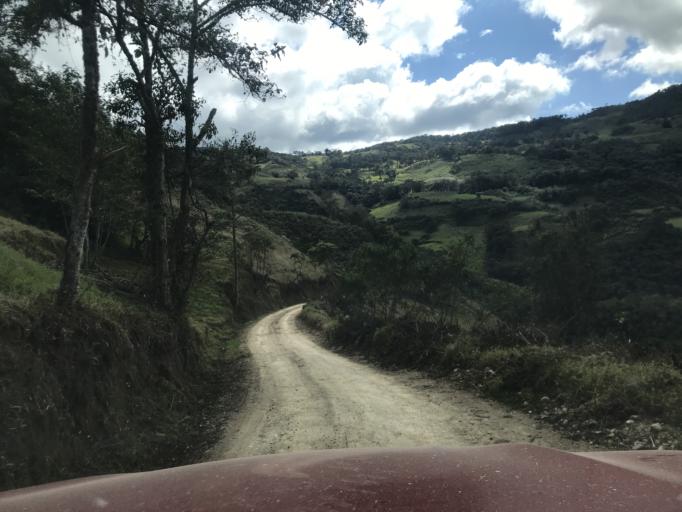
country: PE
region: Cajamarca
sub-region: Provincia de Chota
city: Querocoto
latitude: -6.3486
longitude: -79.0564
